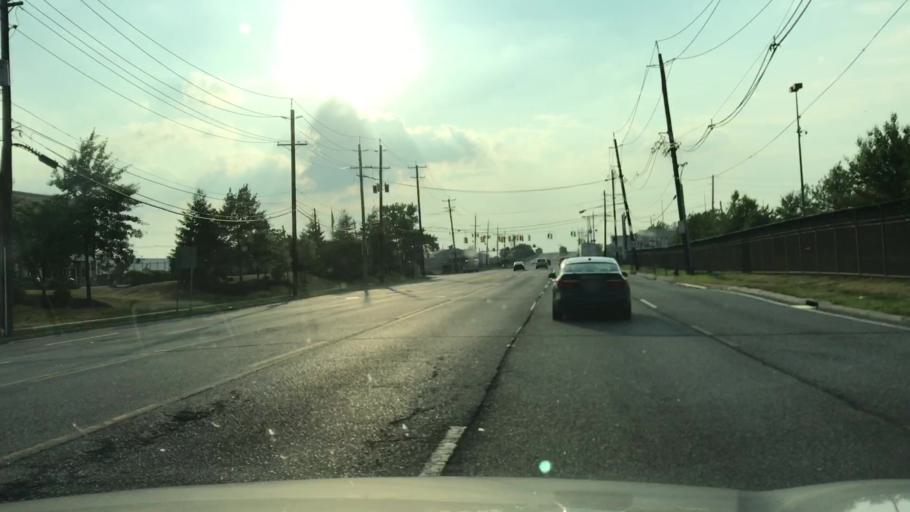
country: US
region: New Jersey
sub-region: Union County
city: Elizabeth
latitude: 40.6665
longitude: -74.1699
